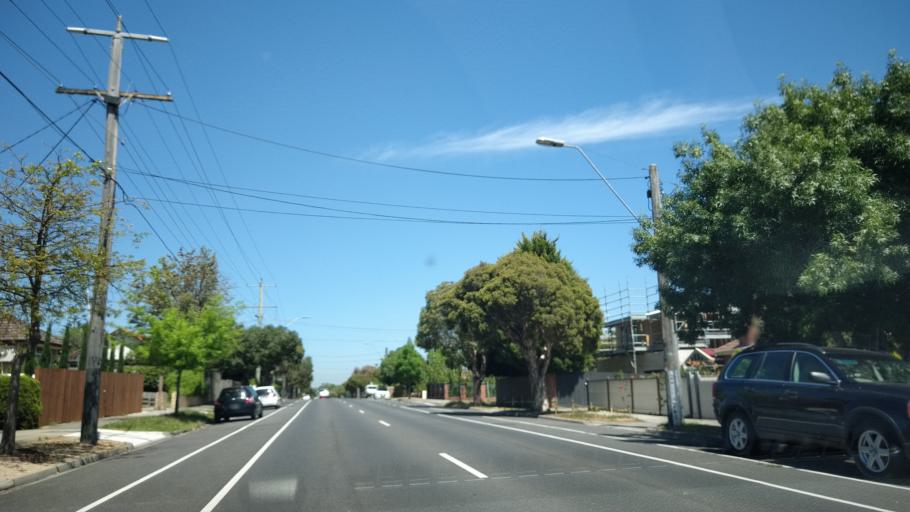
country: AU
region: Victoria
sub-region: Glen Eira
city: Caulfield South
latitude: -37.8991
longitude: 145.0266
